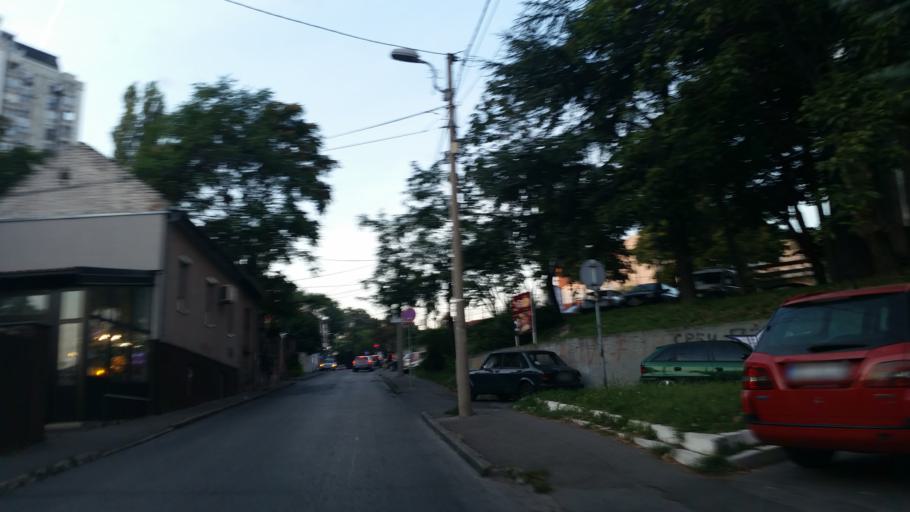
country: RS
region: Central Serbia
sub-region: Belgrade
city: Vracar
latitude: 44.7945
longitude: 20.4901
